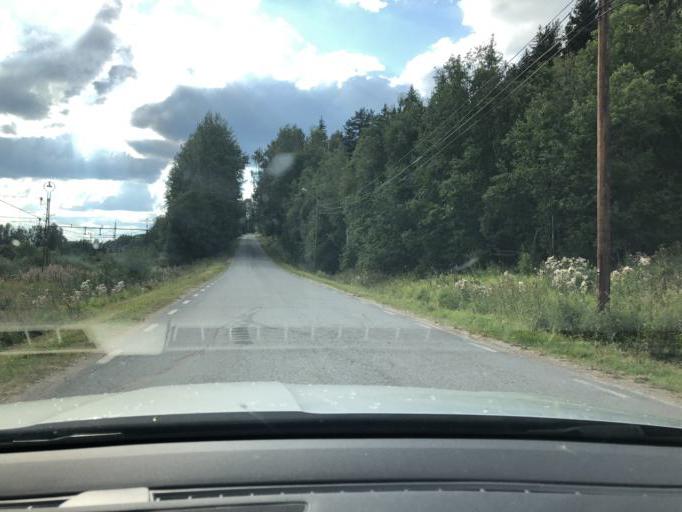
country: SE
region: Vaesternorrland
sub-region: Solleftea Kommun
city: Solleftea
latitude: 63.2117
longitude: 17.1856
